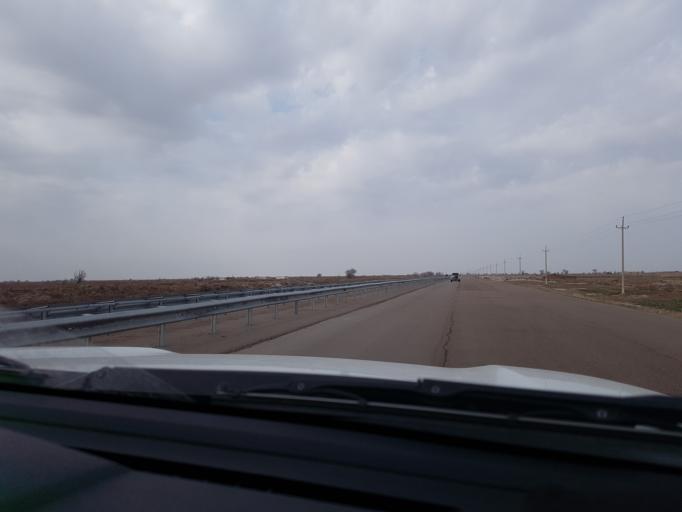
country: TM
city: Akdepe
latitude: 41.7367
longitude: 59.1146
